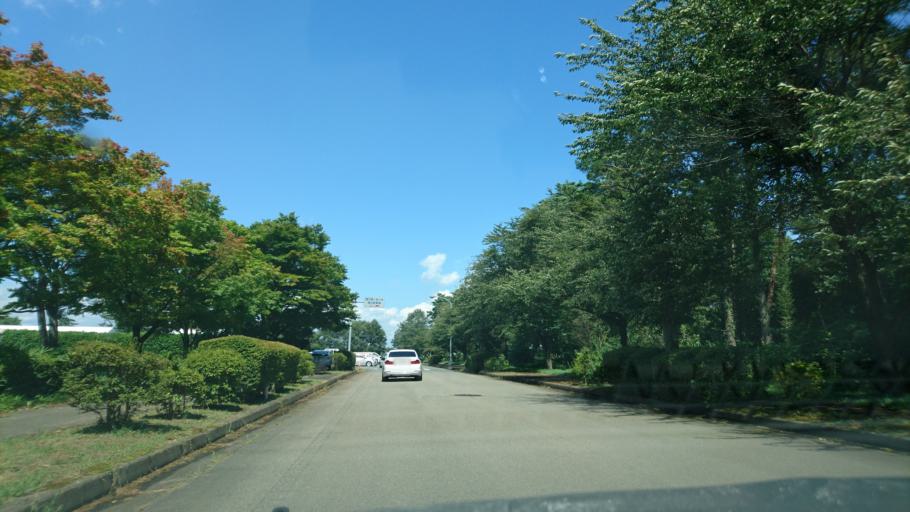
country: JP
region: Iwate
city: Morioka-shi
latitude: 39.8092
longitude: 141.1332
